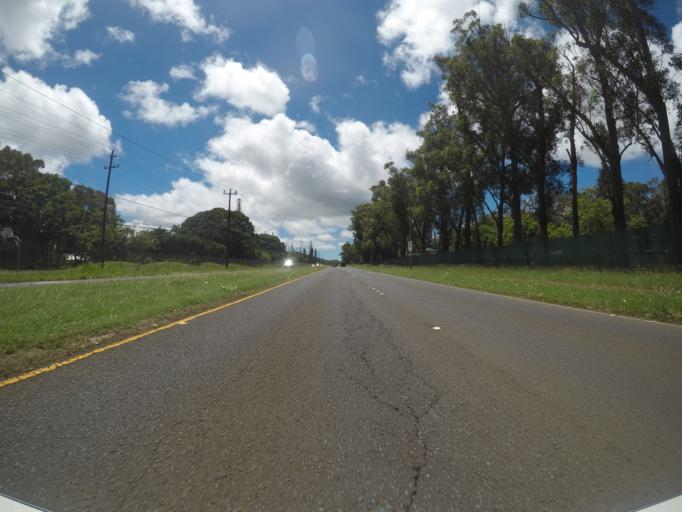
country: US
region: Hawaii
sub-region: Honolulu County
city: Schofield Barracks
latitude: 21.4912
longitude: -158.0457
